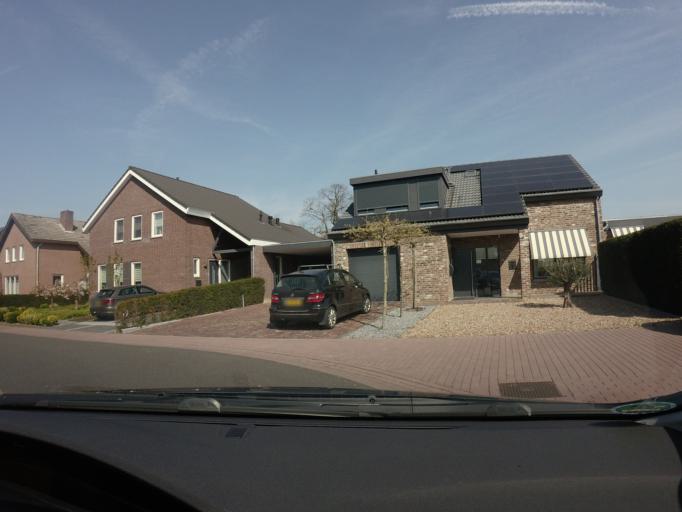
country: NL
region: Limburg
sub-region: Valkenburg aan de Geul
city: Berg
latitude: 50.8462
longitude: 5.7614
